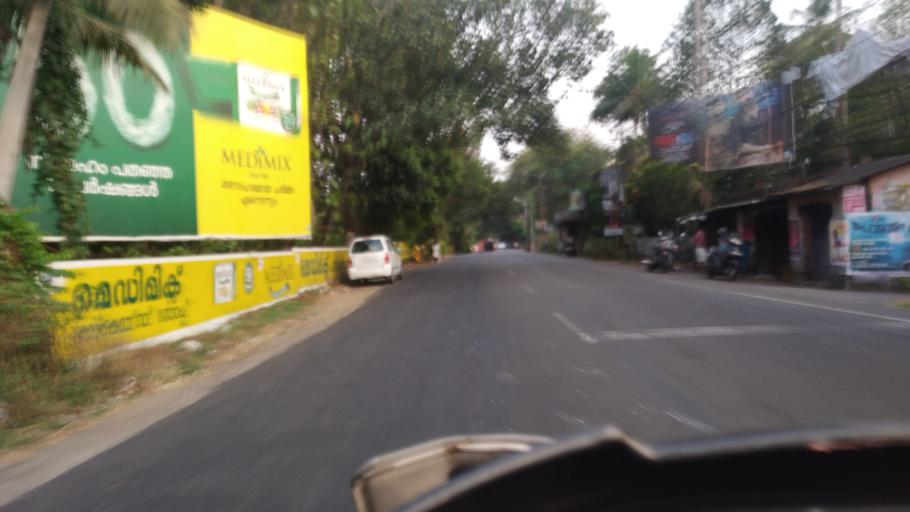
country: IN
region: Kerala
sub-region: Thrissur District
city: Kodungallur
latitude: 10.2479
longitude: 76.1887
